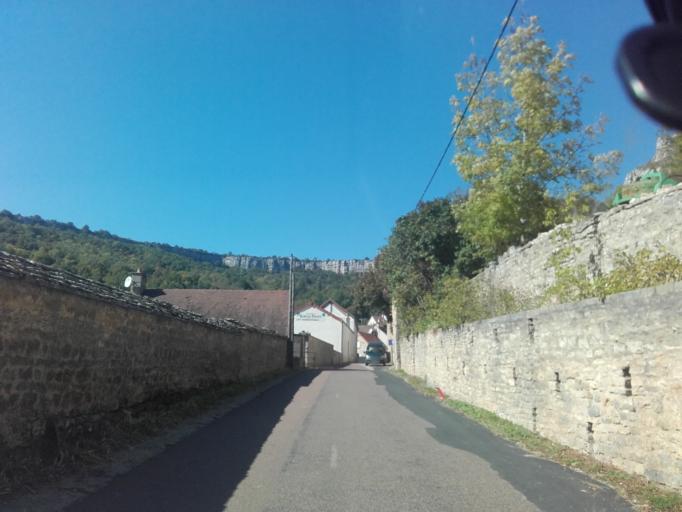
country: FR
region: Bourgogne
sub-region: Departement de la Cote-d'Or
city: Meursault
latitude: 46.9957
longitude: 4.7106
